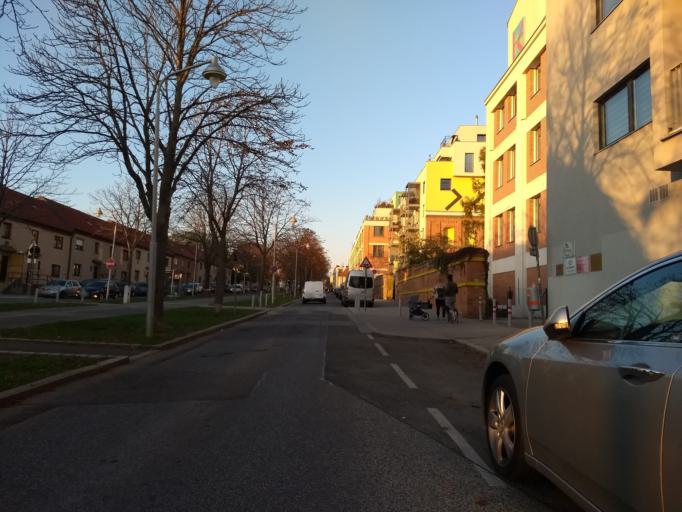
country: AT
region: Lower Austria
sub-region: Politischer Bezirk Modling
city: Vosendorf
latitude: 48.1659
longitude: 16.3242
